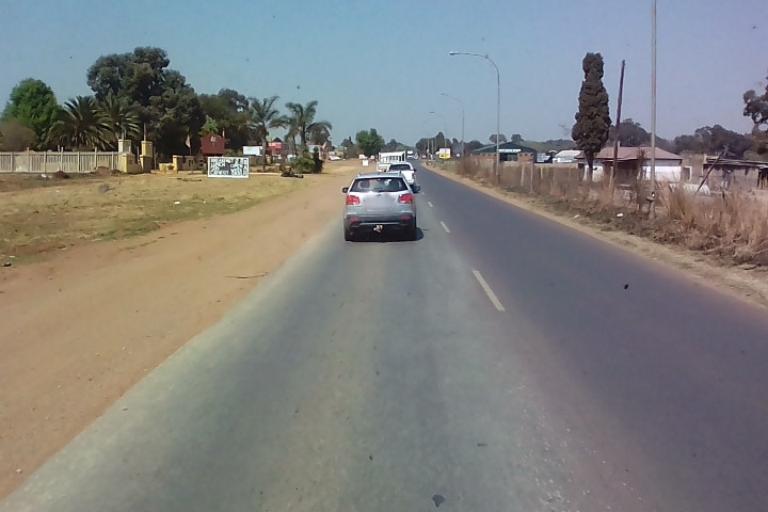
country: ZA
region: Gauteng
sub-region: Ekurhuleni Metropolitan Municipality
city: Benoni
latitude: -26.1054
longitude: 28.2962
